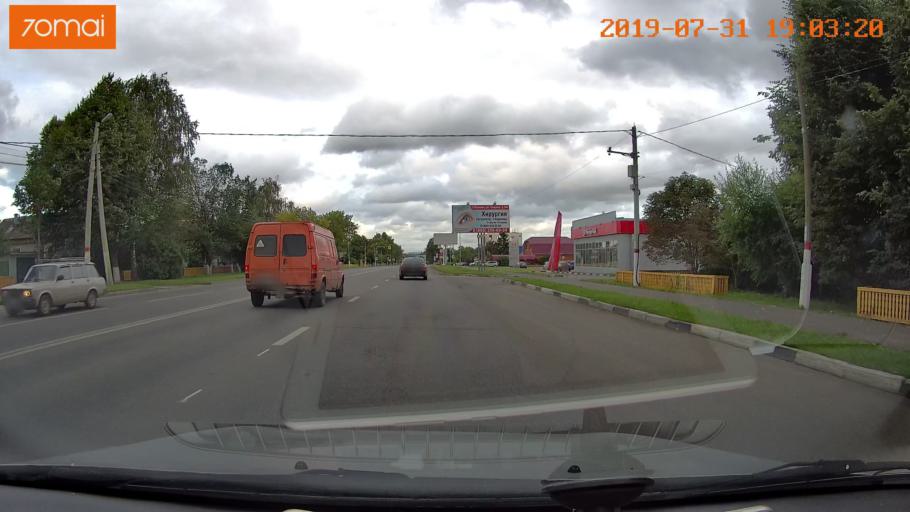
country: RU
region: Moskovskaya
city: Raduzhnyy
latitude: 55.1152
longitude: 38.7370
